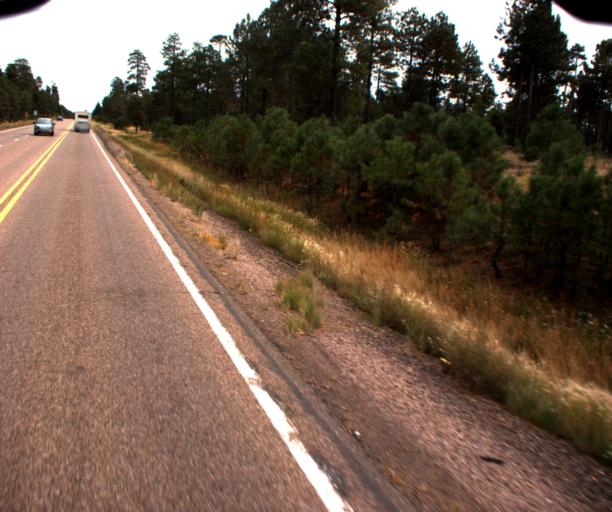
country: US
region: Arizona
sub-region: Navajo County
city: Heber-Overgaard
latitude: 34.3270
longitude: -110.8224
